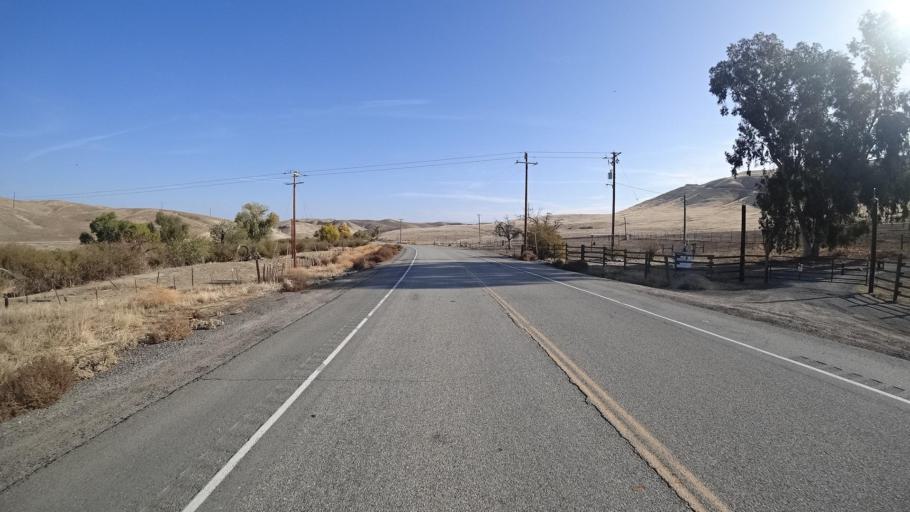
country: US
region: California
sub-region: Kern County
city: Oildale
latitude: 35.5273
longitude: -118.9693
